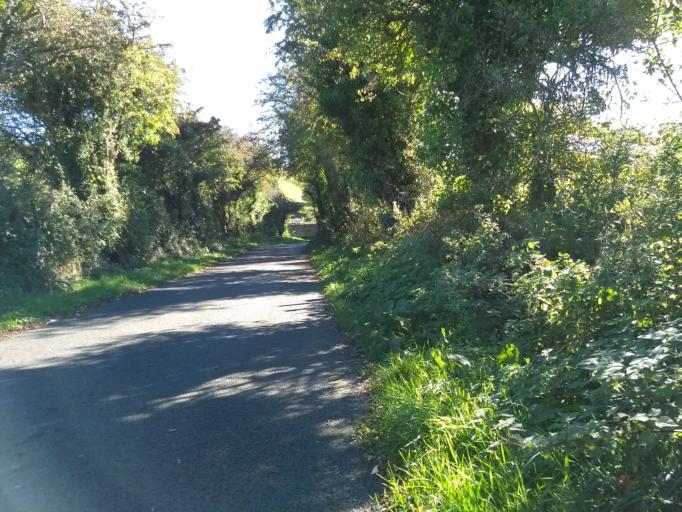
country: GB
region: England
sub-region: Isle of Wight
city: Ventnor
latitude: 50.6053
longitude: -1.2292
